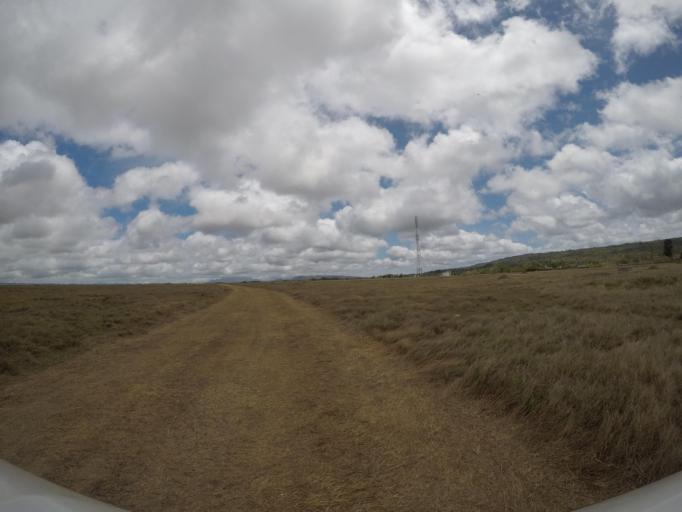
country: TL
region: Lautem
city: Lospalos
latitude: -8.4433
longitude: 126.9900
